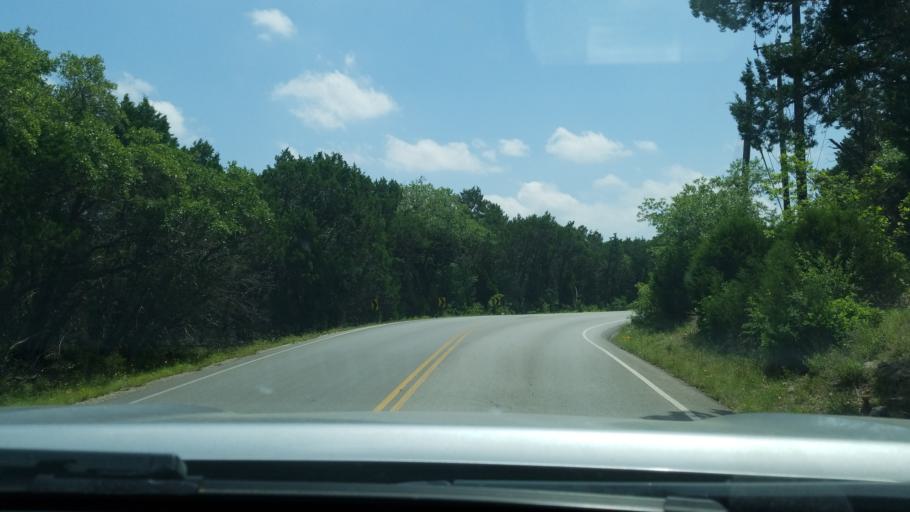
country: US
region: Texas
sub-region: Hays County
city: Woodcreek
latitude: 30.0232
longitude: -98.1302
